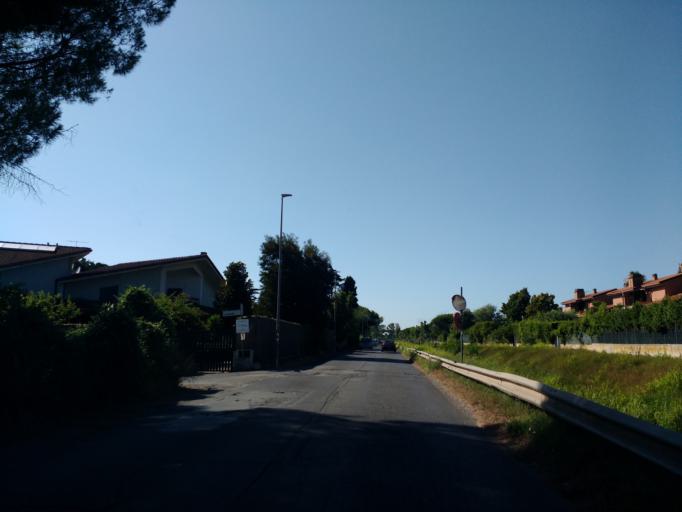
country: IT
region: Latium
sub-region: Citta metropolitana di Roma Capitale
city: Acilia-Castel Fusano-Ostia Antica
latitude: 41.7460
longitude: 12.3349
